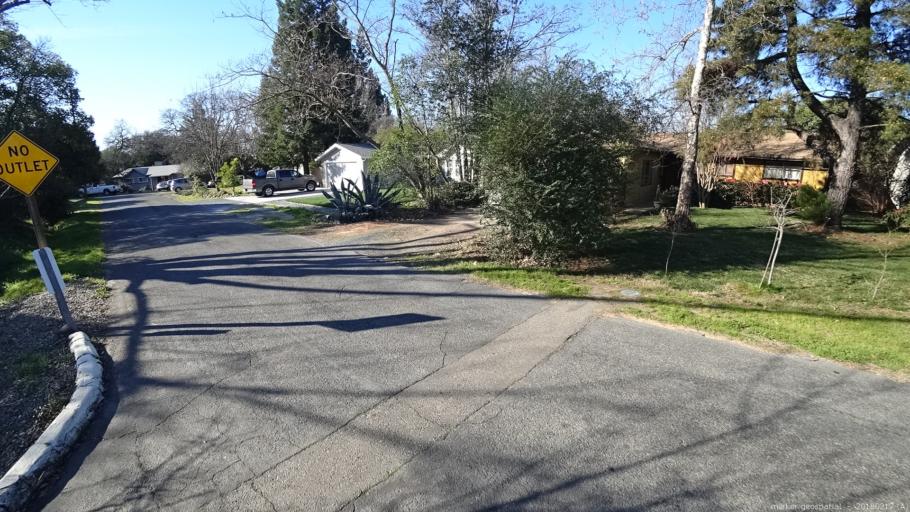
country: US
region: California
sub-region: Sacramento County
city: Orangevale
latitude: 38.6693
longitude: -121.2012
